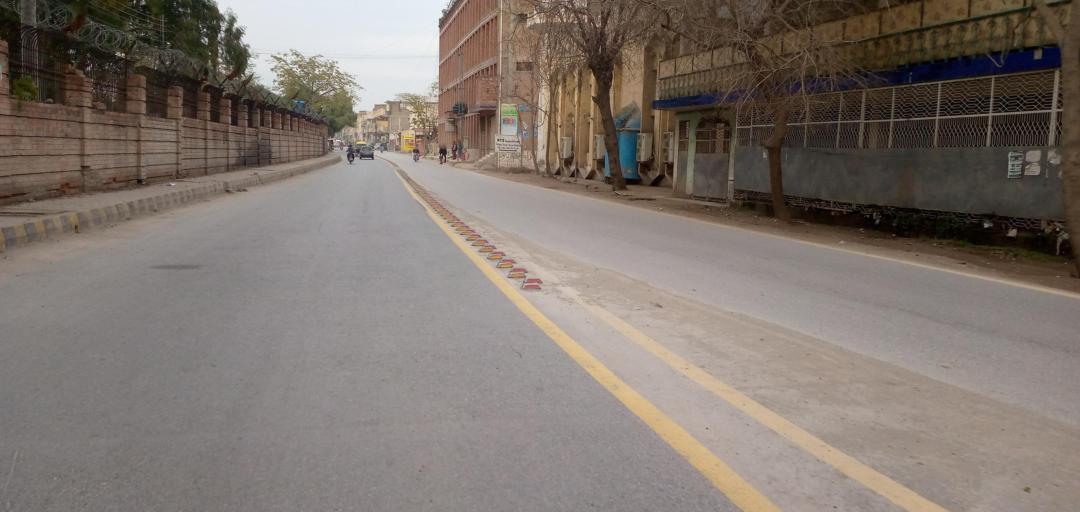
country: PK
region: Khyber Pakhtunkhwa
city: Peshawar
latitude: 34.0195
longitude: 71.4895
